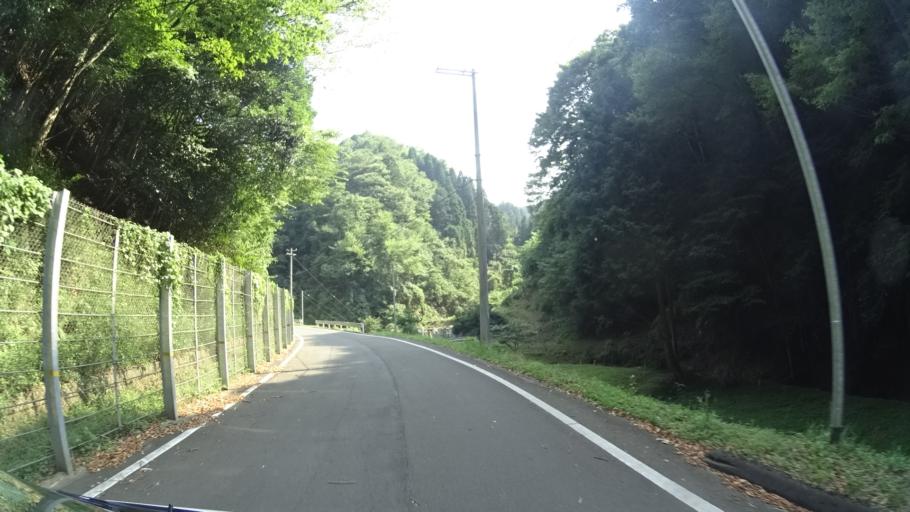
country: JP
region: Kyoto
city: Maizuru
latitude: 35.4041
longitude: 135.2409
